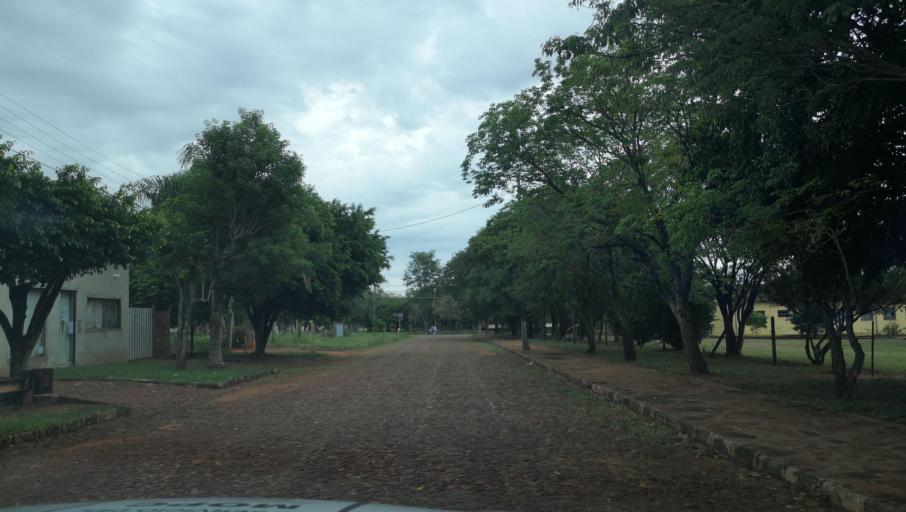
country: PY
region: Misiones
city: Santa Maria
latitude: -26.8862
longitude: -57.0369
